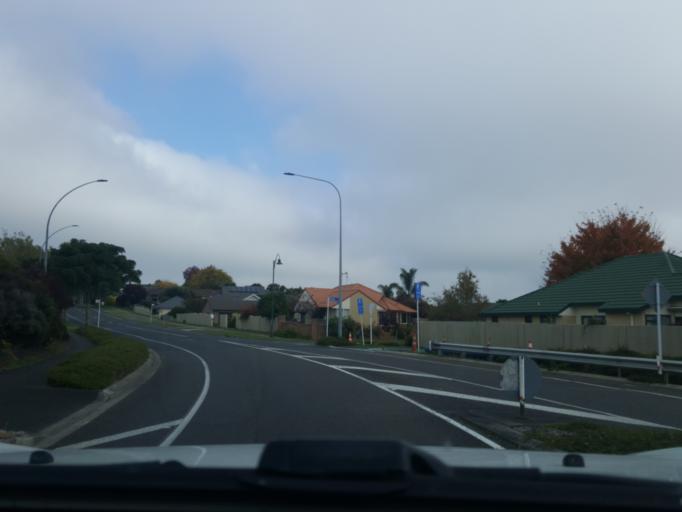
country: NZ
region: Waikato
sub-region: Hamilton City
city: Hamilton
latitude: -37.7509
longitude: 175.2929
